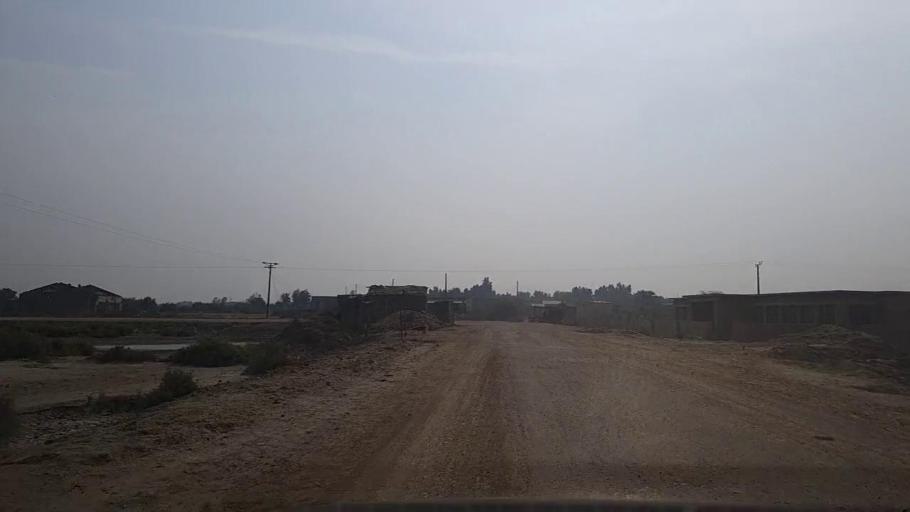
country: PK
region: Sindh
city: Mirpur Sakro
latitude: 24.4034
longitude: 67.7429
